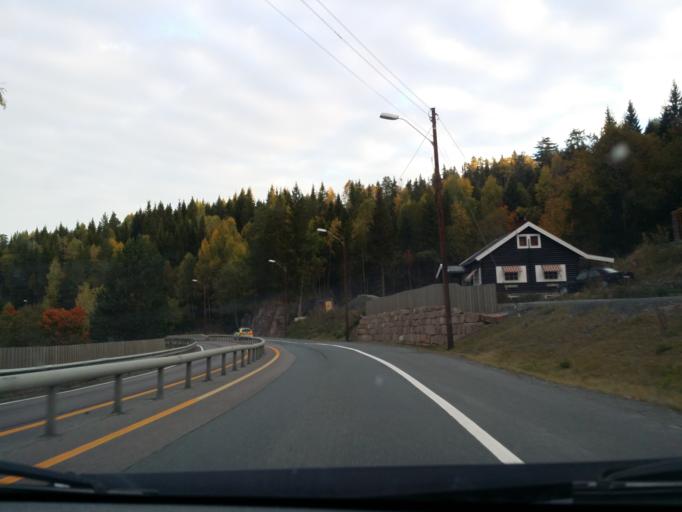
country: NO
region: Buskerud
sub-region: Hole
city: Vik
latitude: 59.9746
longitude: 10.3328
